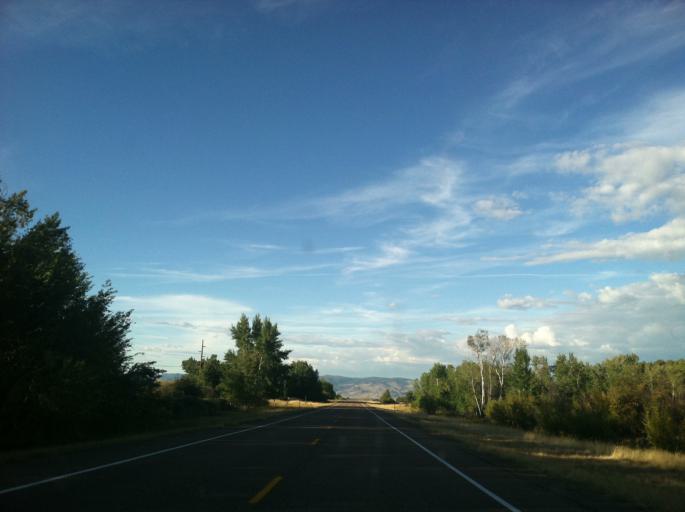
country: US
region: Montana
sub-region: Granite County
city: Philipsburg
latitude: 46.5313
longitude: -113.2233
